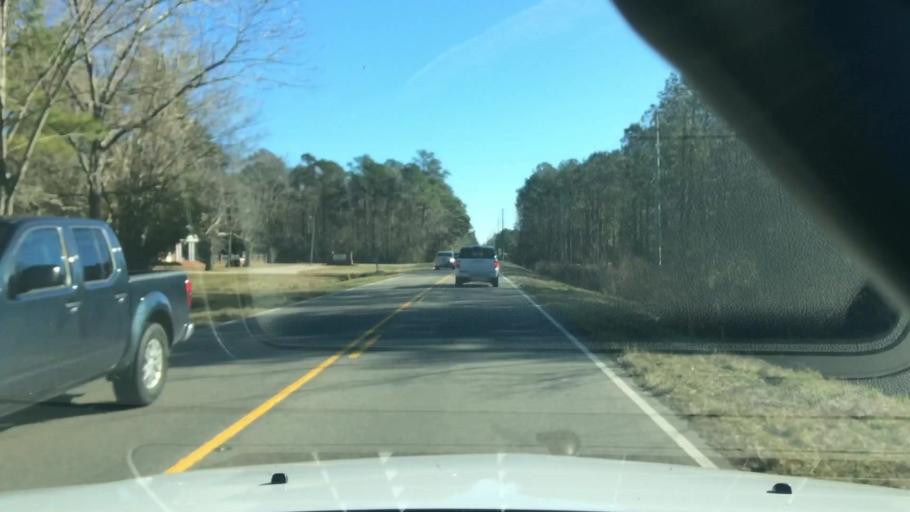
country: US
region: North Carolina
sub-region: Brunswick County
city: Carolina Shores
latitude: 33.9309
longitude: -78.6074
